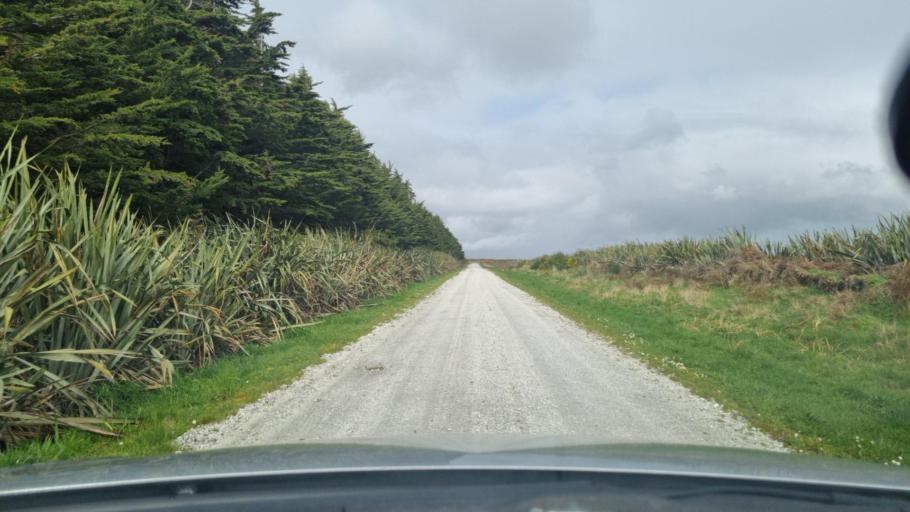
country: NZ
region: Southland
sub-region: Invercargill City
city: Bluff
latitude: -46.5154
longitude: 168.3588
